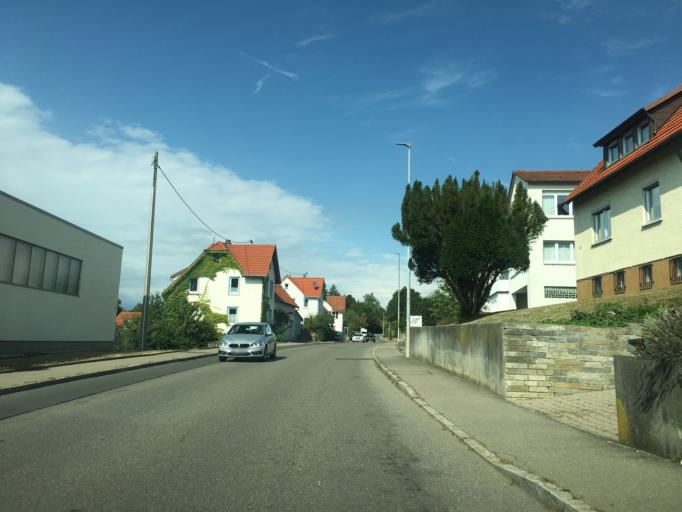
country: DE
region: Baden-Wuerttemberg
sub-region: Tuebingen Region
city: Gomaringen
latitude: 48.4377
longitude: 9.1481
